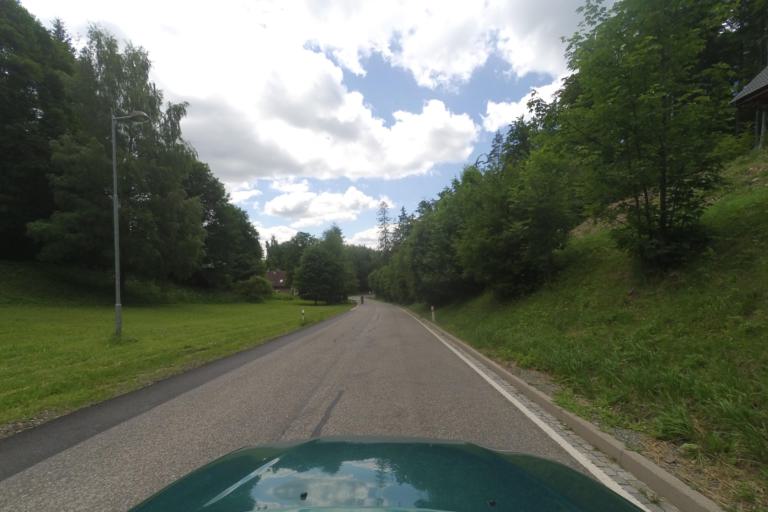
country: PL
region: Lower Silesian Voivodeship
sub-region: Powiat klodzki
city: Lewin Klodzki
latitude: 50.3536
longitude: 16.2446
